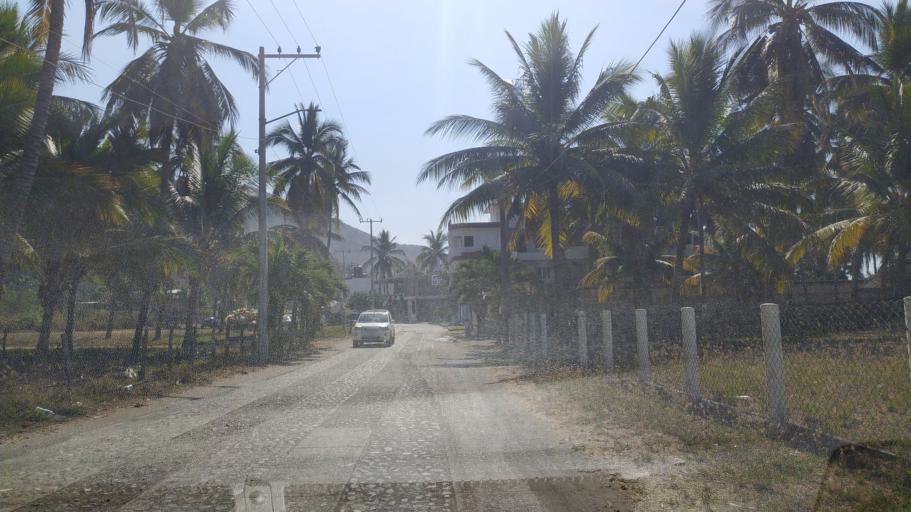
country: MX
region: Michoacan
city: Coahuayana Viejo
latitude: 18.5822
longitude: -103.6726
